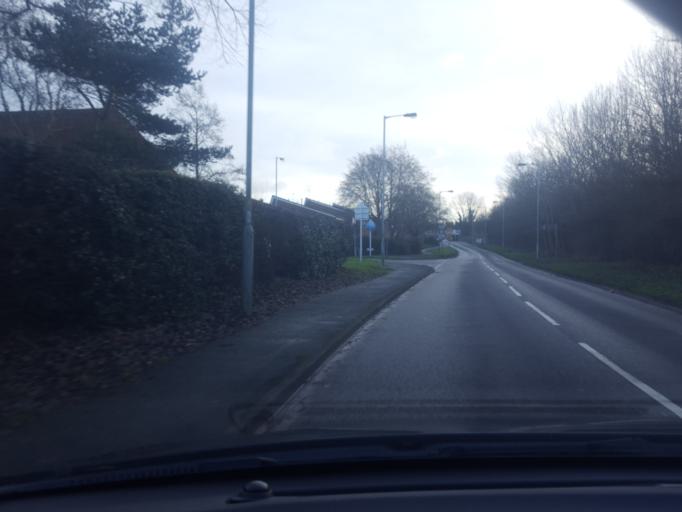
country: GB
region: England
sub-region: Staffordshire
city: Codsall
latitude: 52.6171
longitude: -2.1613
